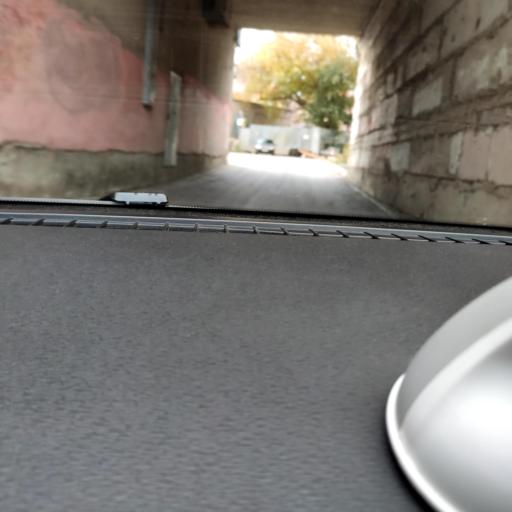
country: RU
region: Samara
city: Petra-Dubrava
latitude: 53.2397
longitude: 50.2763
